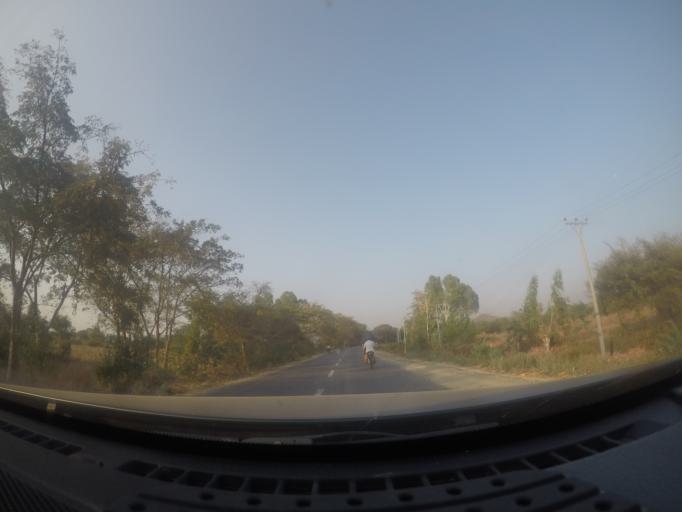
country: MM
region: Mandalay
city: Yamethin
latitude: 20.7336
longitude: 96.2052
